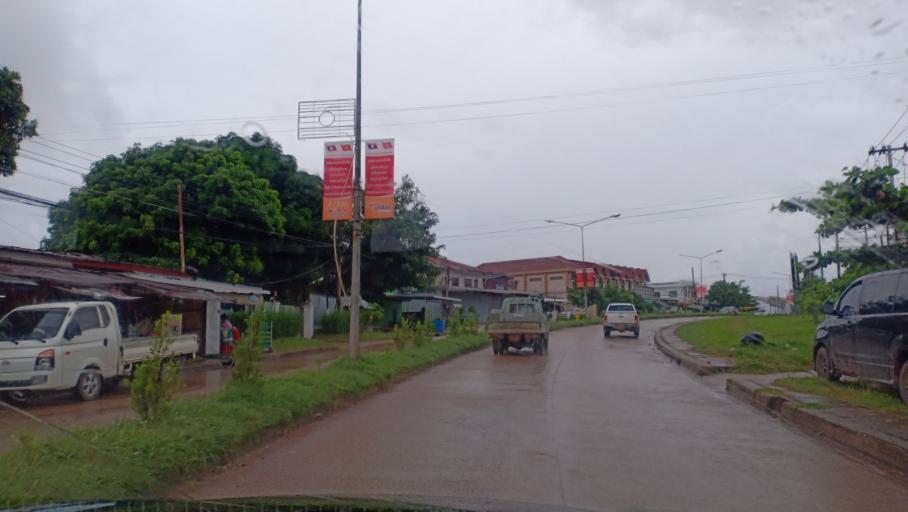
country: LA
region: Khammouan
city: Thakhek
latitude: 17.4024
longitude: 104.8245
